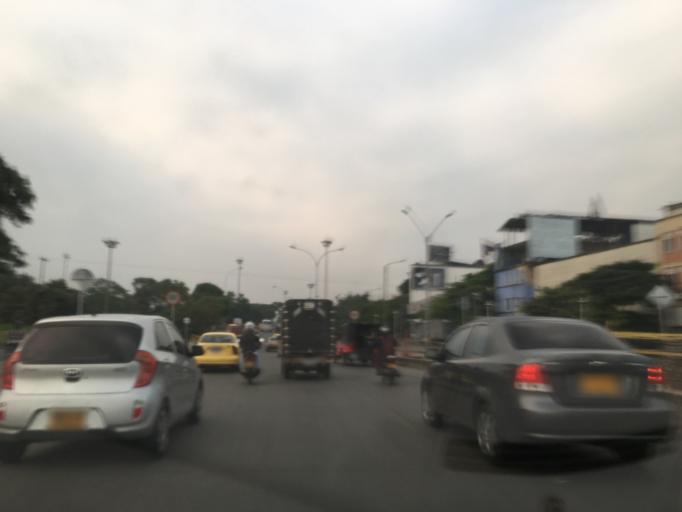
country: CO
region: Valle del Cauca
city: Cali
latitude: 3.4621
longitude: -76.5218
